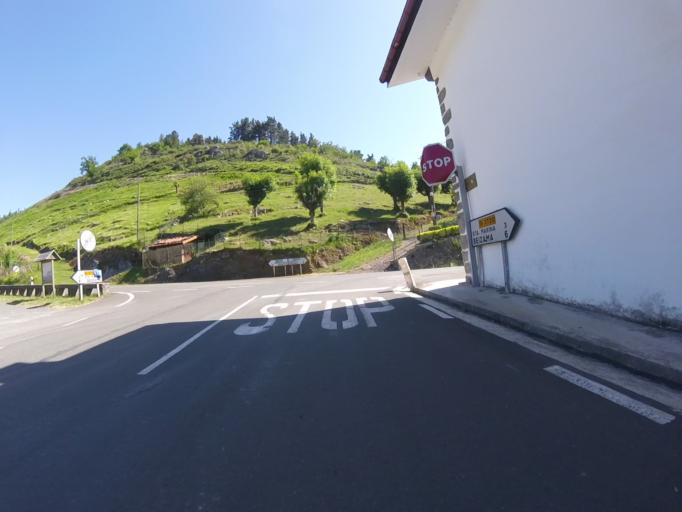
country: ES
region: Basque Country
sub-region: Provincia de Guipuzcoa
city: Albiztur
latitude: 43.1217
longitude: -2.1526
